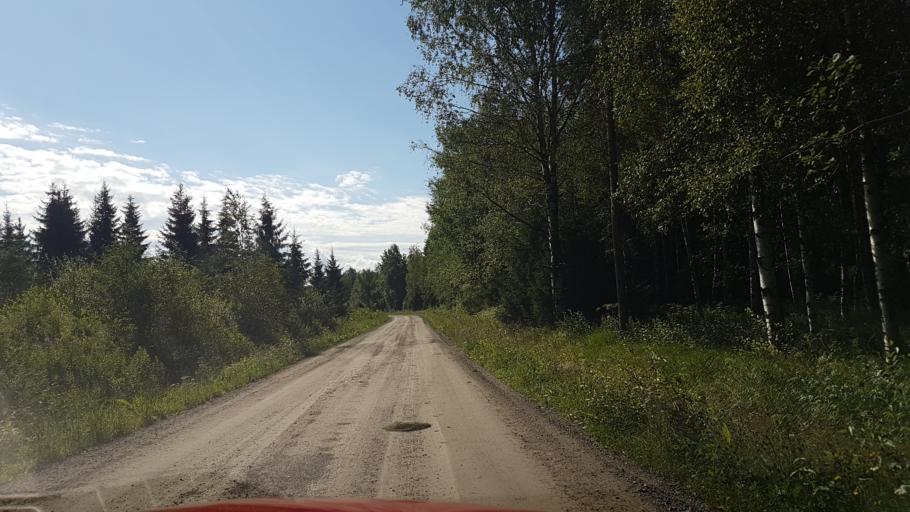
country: FI
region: Northern Ostrobothnia
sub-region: Ylivieska
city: Himanka
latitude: 64.0774
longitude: 23.8042
